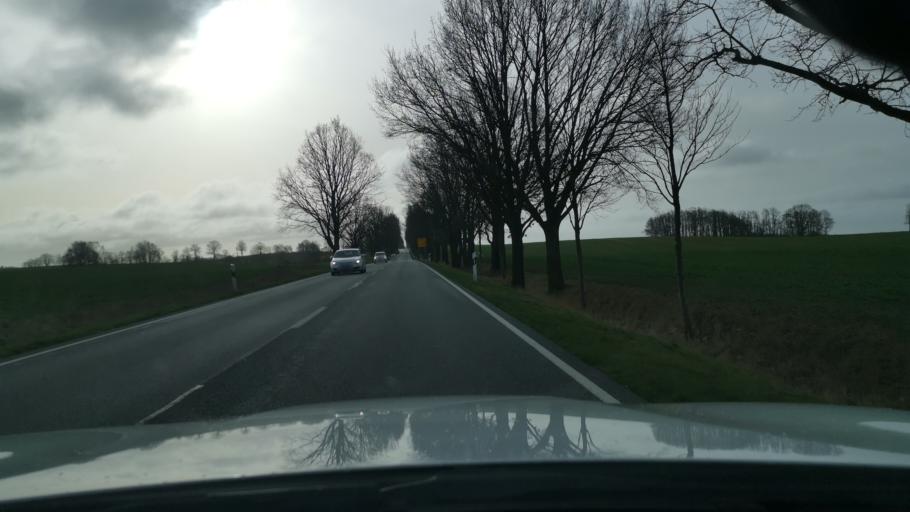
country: DE
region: Mecklenburg-Vorpommern
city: Laage
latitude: 53.9635
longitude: 12.2938
